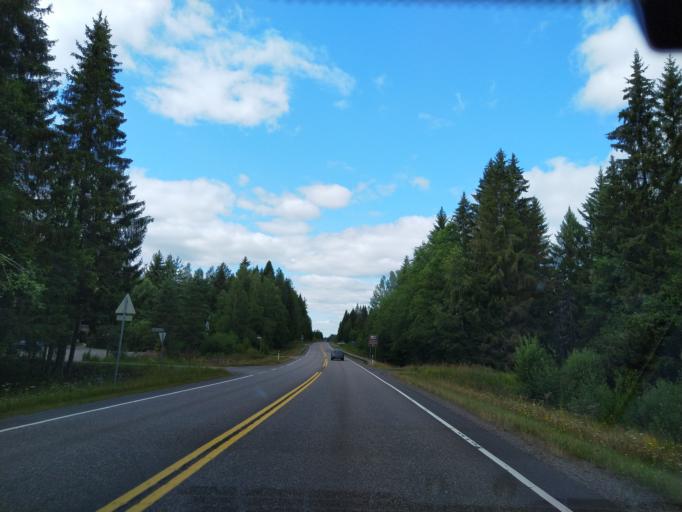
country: FI
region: Haeme
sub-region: Haemeenlinna
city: Renko
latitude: 60.7609
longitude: 24.2870
